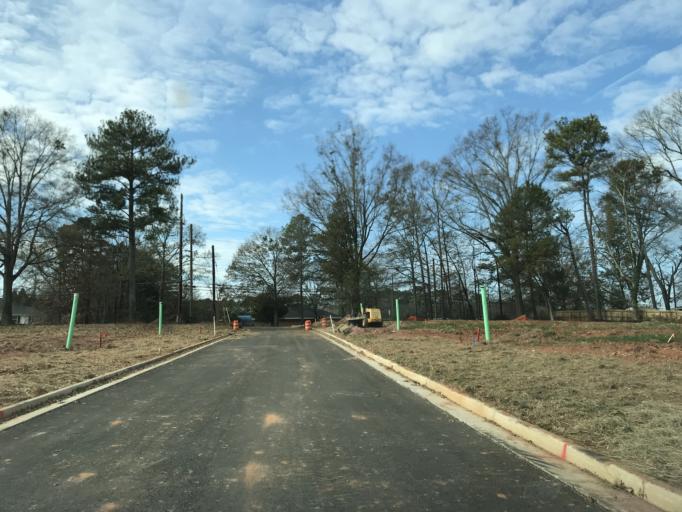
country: US
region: Georgia
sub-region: DeKalb County
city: Clarkston
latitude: 33.8230
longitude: -84.2498
